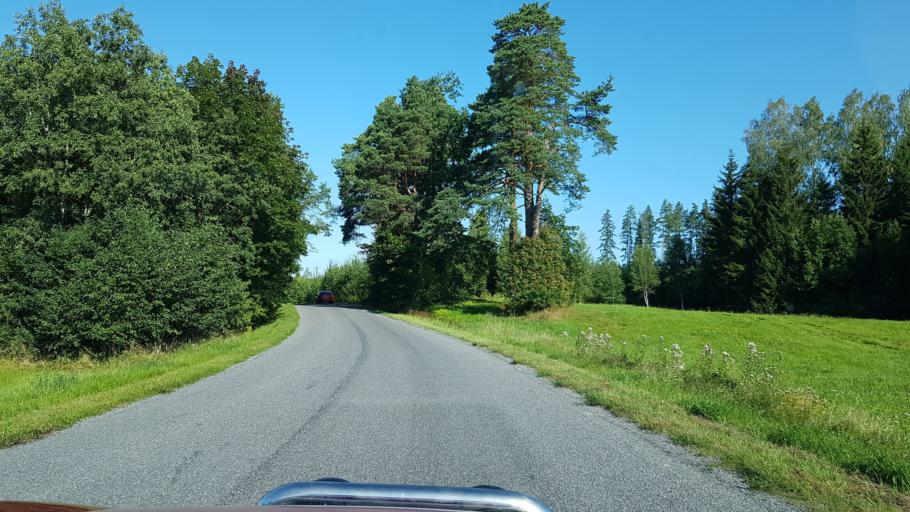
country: EE
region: Vorumaa
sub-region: Voru linn
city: Voru
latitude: 57.7363
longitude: 26.9268
